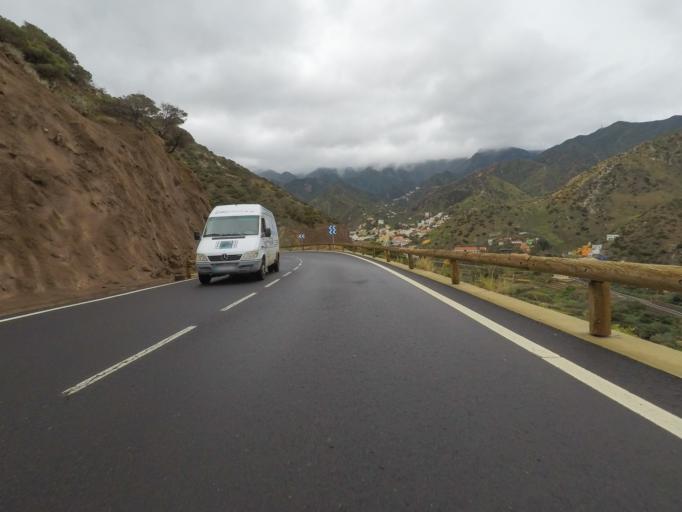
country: ES
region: Canary Islands
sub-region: Provincia de Santa Cruz de Tenerife
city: Vallehermosa
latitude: 28.1873
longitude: -17.2604
